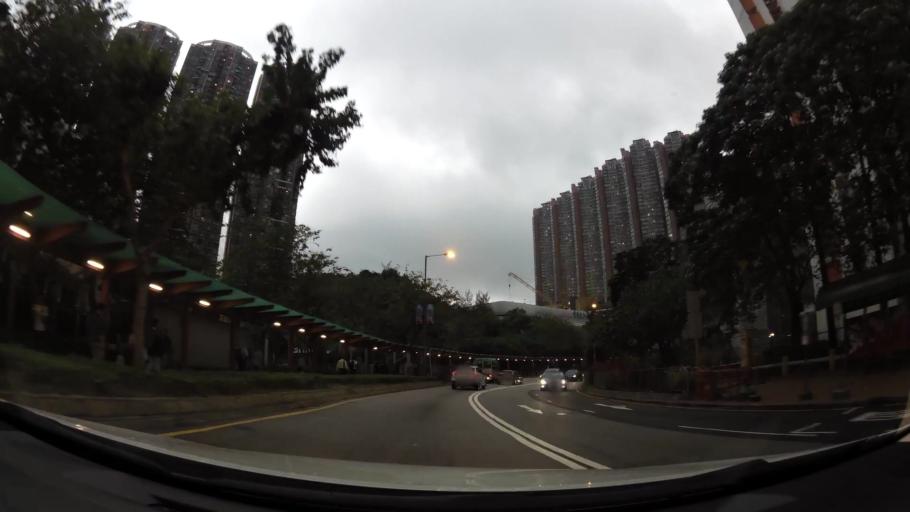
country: HK
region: Tsuen Wan
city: Tsuen Wan
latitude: 22.3612
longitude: 114.1053
